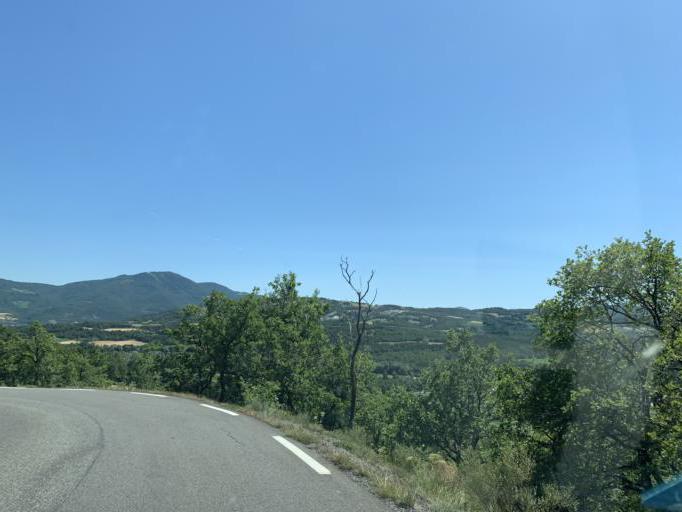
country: FR
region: Provence-Alpes-Cote d'Azur
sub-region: Departement des Hautes-Alpes
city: La Batie-Neuve
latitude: 44.5804
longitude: 6.1752
